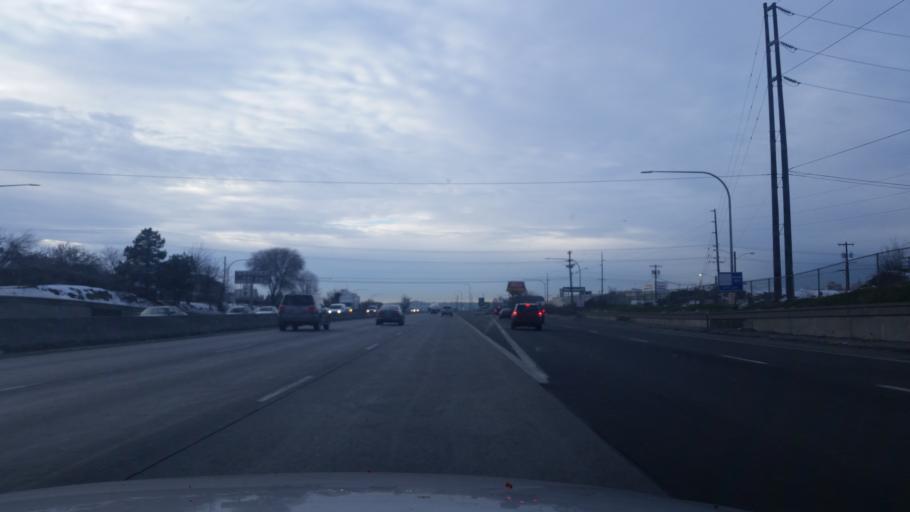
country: US
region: Washington
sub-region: Spokane County
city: Spokane
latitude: 47.6524
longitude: -117.4059
